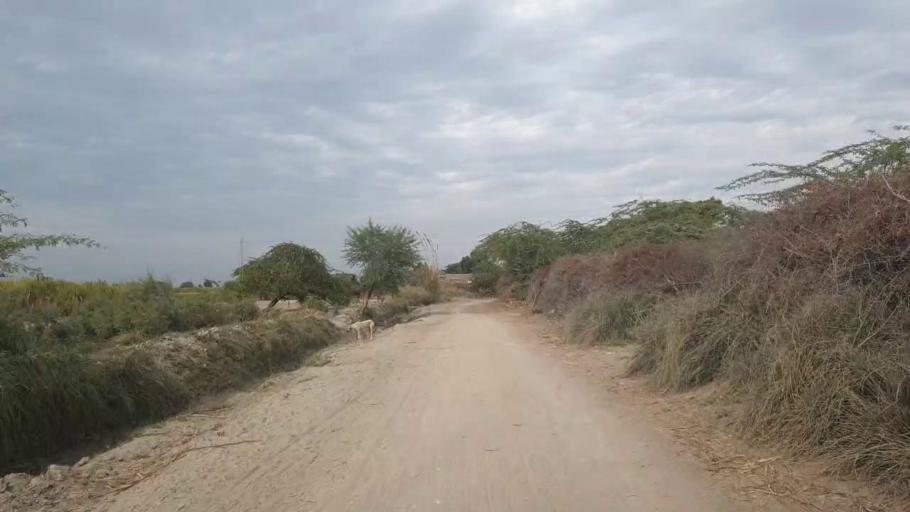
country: PK
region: Sindh
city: Sinjhoro
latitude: 26.0256
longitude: 68.8738
